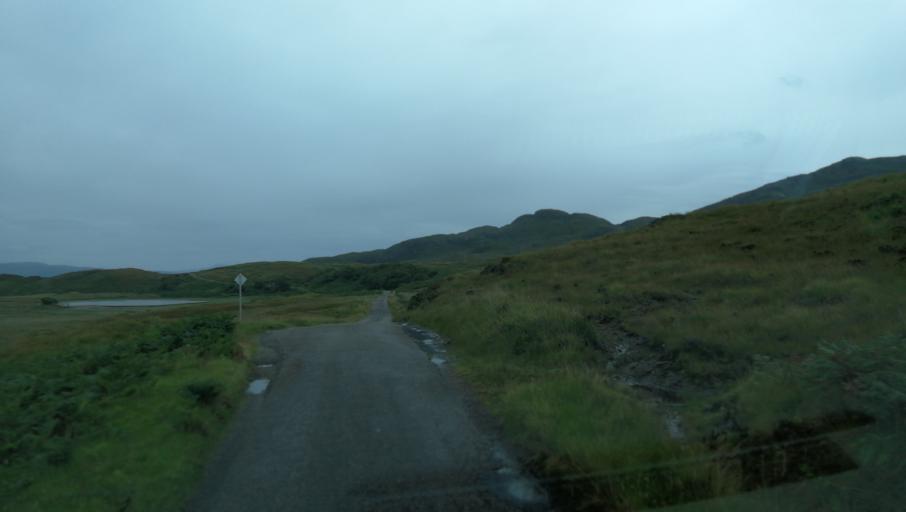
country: GB
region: Scotland
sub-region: Argyll and Bute
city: Isle Of Mull
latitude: 56.7165
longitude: -6.1498
